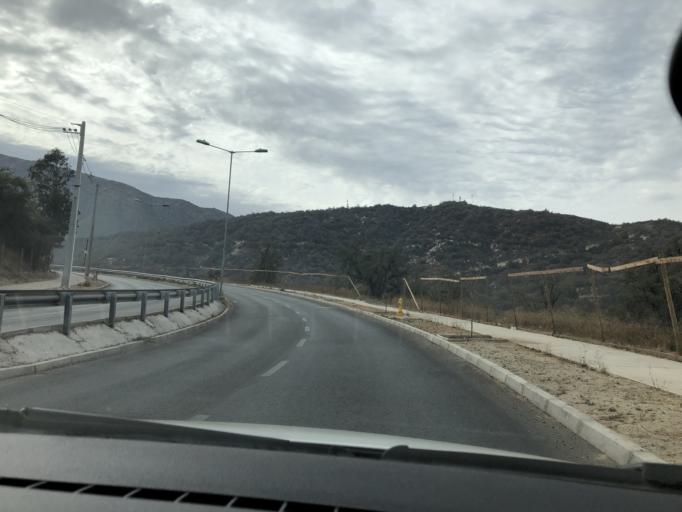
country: CL
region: Santiago Metropolitan
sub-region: Provincia de Cordillera
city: Puente Alto
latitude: -33.5932
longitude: -70.5080
